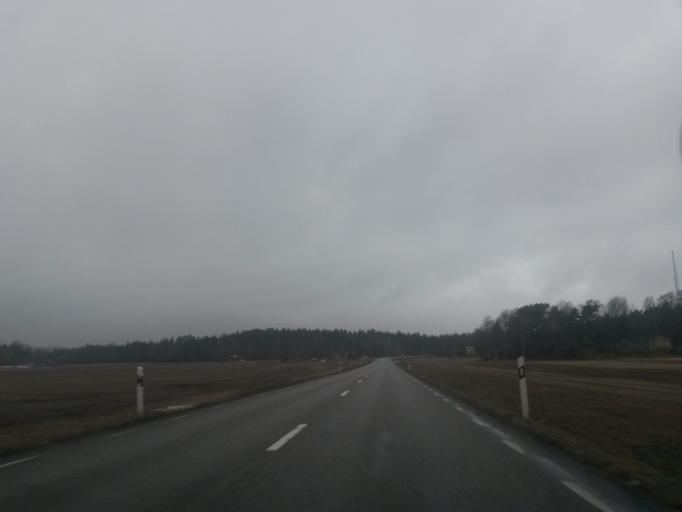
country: SE
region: Vaestra Goetaland
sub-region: Alingsas Kommun
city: Sollebrunn
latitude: 58.1239
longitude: 12.5112
